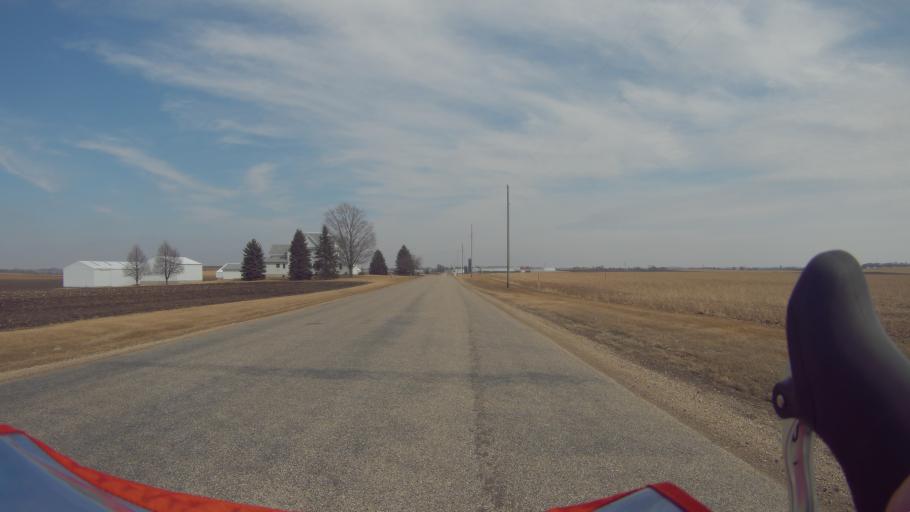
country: US
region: Wisconsin
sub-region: Dane County
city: Waunakee
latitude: 43.1774
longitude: -89.4963
